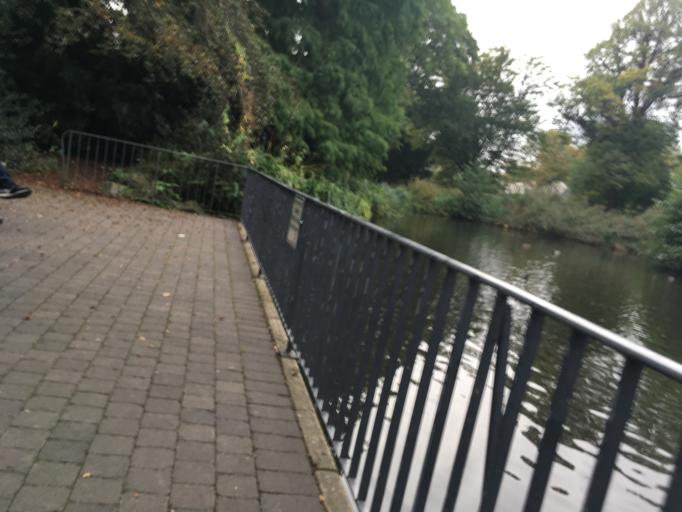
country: DE
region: North Rhine-Westphalia
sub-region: Regierungsbezirk Dusseldorf
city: Essen
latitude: 51.4892
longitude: 7.0126
